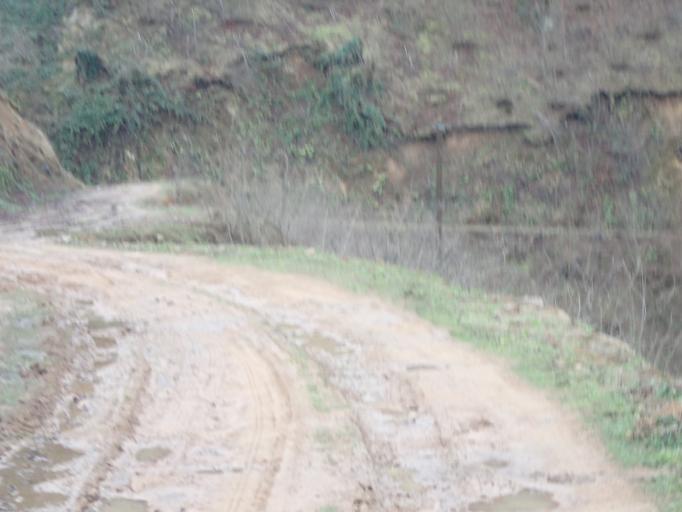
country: TR
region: Ordu
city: Camas
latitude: 40.8587
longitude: 37.5155
